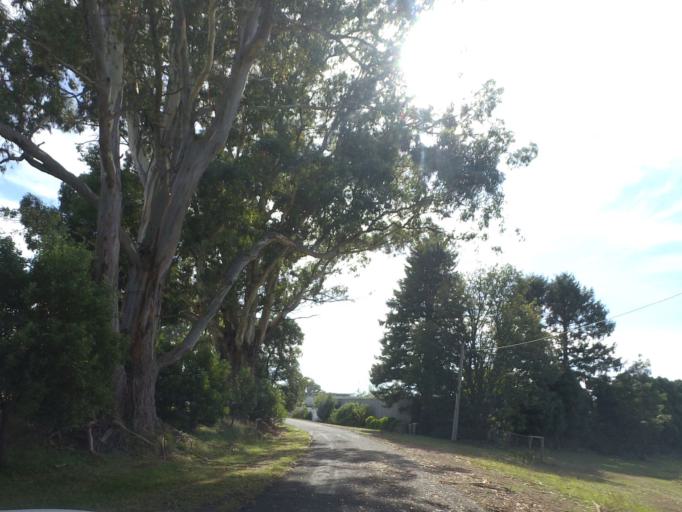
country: AU
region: Victoria
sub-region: Moorabool
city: Bacchus Marsh
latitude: -37.4014
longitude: 144.2540
